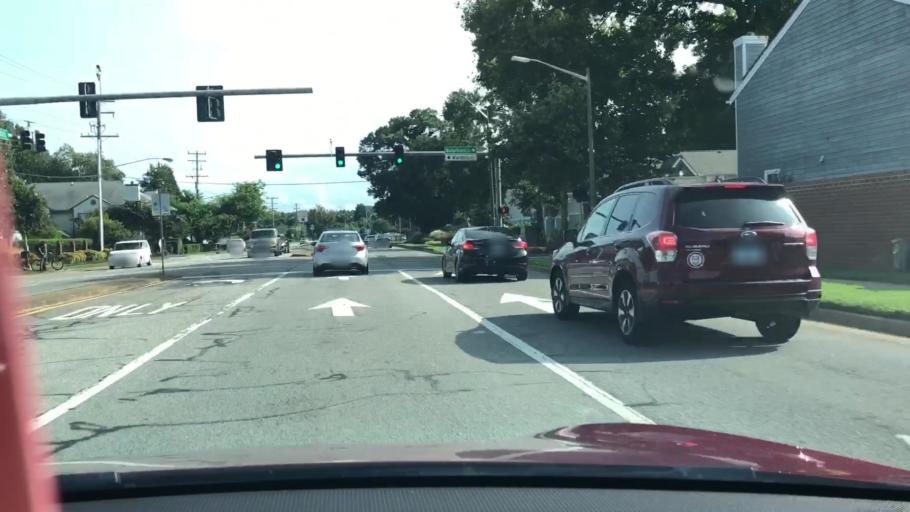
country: US
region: Virginia
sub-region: City of Virginia Beach
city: Virginia Beach
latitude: 36.8507
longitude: -75.9944
